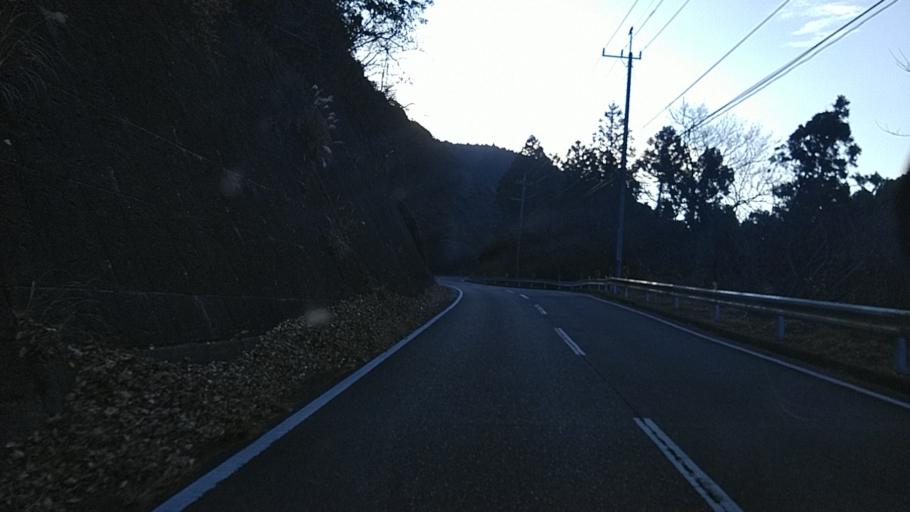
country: JP
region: Chiba
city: Kimitsu
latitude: 35.2655
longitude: 139.9296
